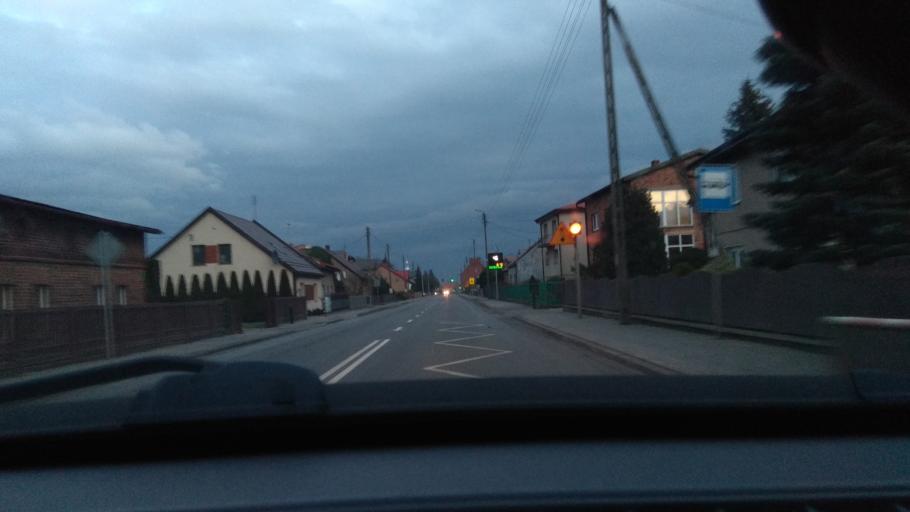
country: PL
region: Greater Poland Voivodeship
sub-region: Powiat kepinski
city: Baranow
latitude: 51.2956
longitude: 18.0438
